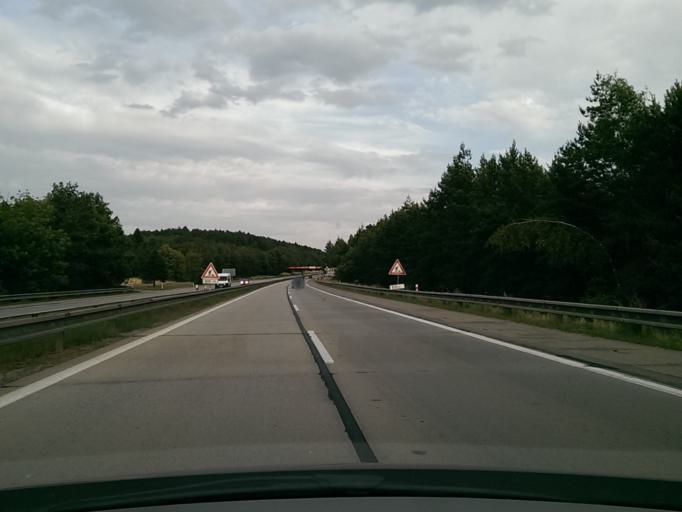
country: CZ
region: Vysocina
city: Krizanov
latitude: 49.3176
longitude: 16.0964
